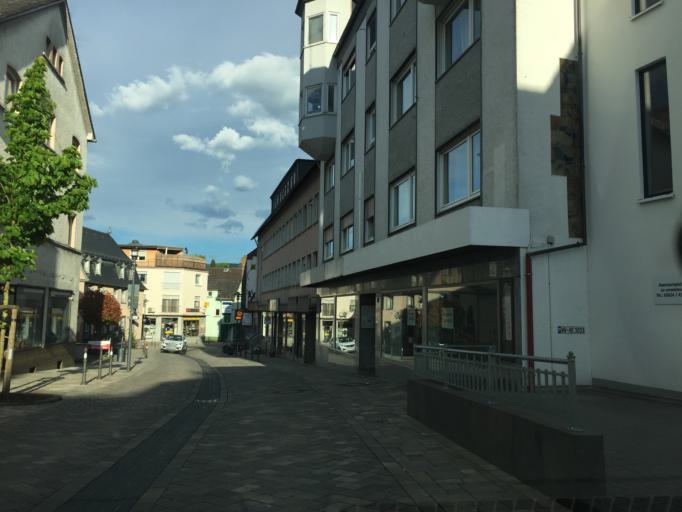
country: DE
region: Rheinland-Pfalz
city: Hohr-Grenzhausen
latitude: 50.4336
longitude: 7.6702
